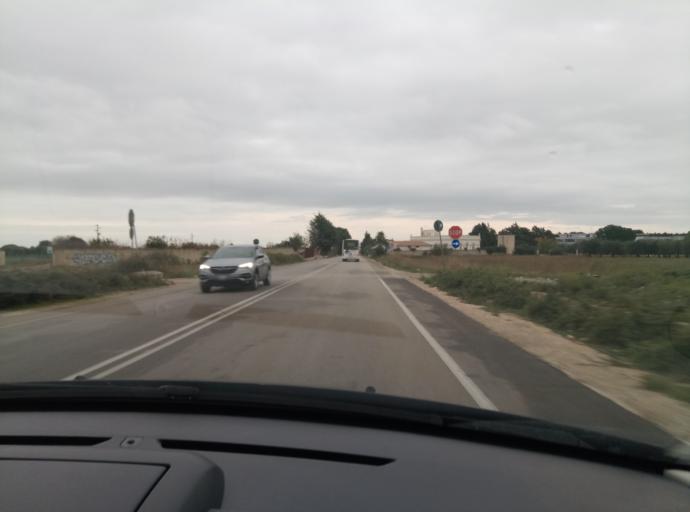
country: IT
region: Apulia
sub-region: Provincia di Bari
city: Acquaviva delle Fonti
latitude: 40.9062
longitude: 16.8454
